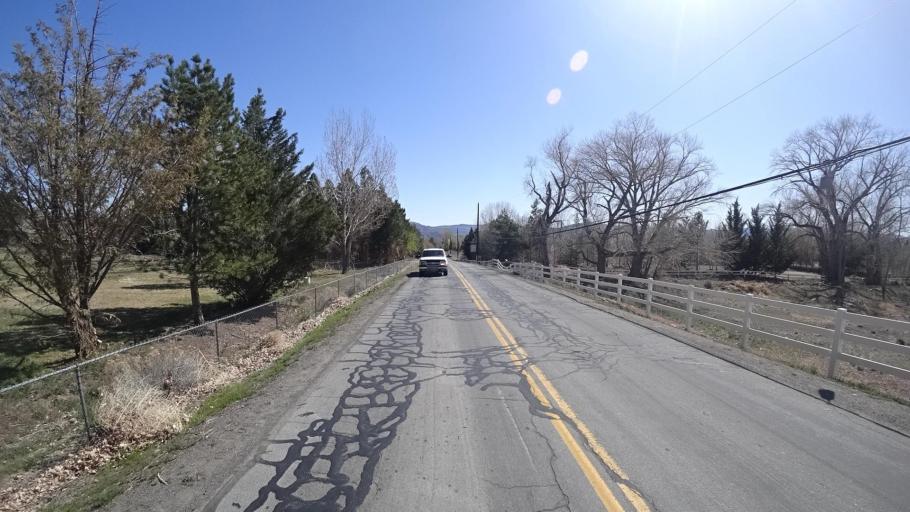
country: US
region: Nevada
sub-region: Washoe County
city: Reno
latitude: 39.4548
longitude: -119.8078
